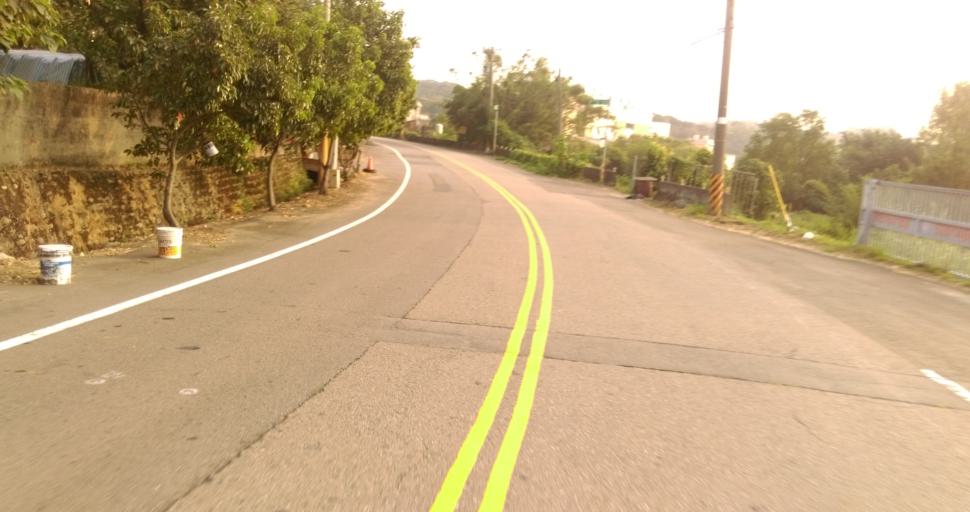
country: TW
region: Taiwan
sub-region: Hsinchu
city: Hsinchu
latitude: 24.7492
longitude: 120.9375
